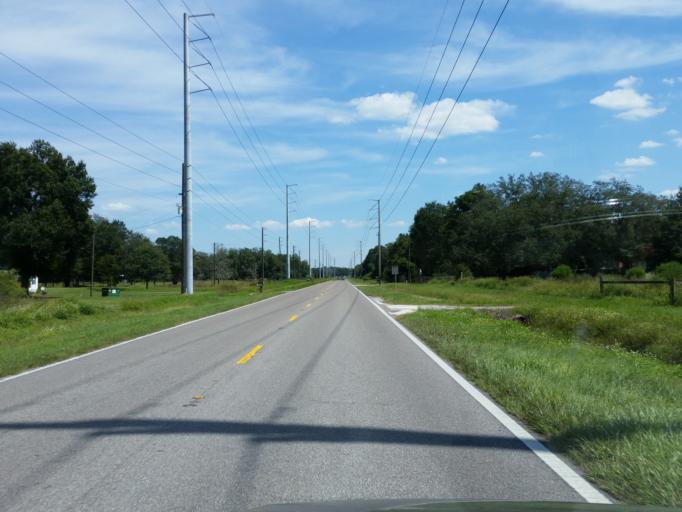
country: US
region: Florida
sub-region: Pasco County
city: Zephyrhills North
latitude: 28.2593
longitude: -82.0888
